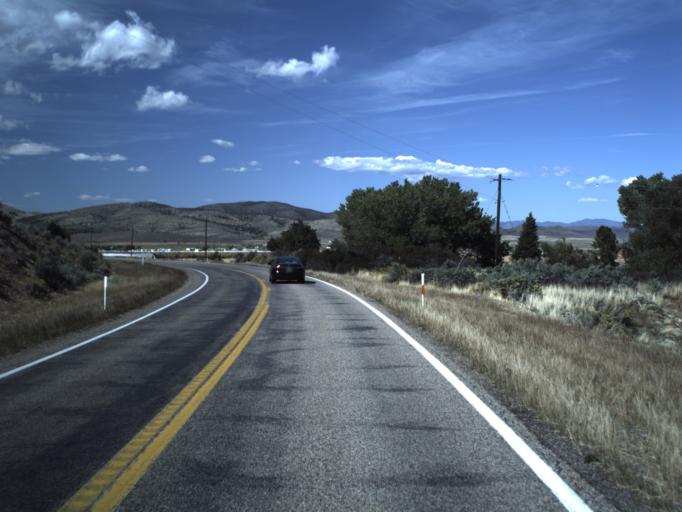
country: US
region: Utah
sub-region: Washington County
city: Enterprise
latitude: 37.5649
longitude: -113.6925
